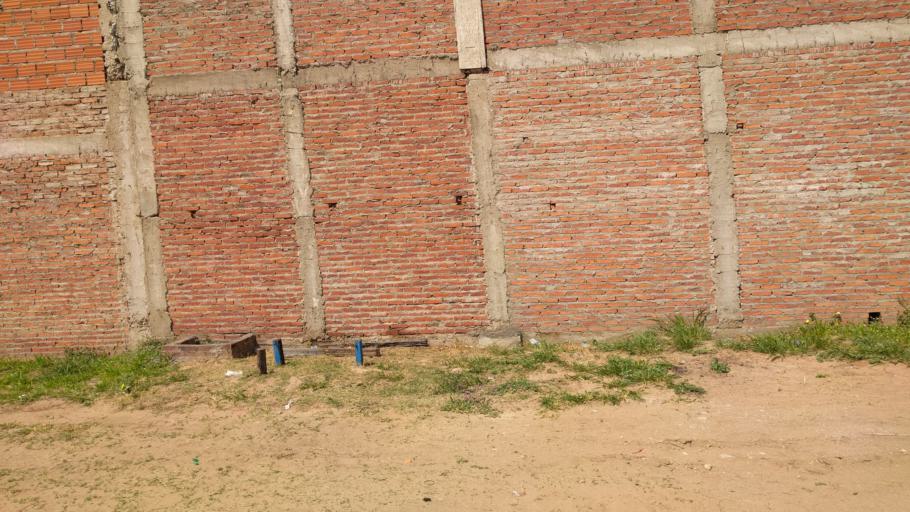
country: BO
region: Santa Cruz
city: Santa Cruz de la Sierra
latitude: -17.6961
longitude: -63.1589
